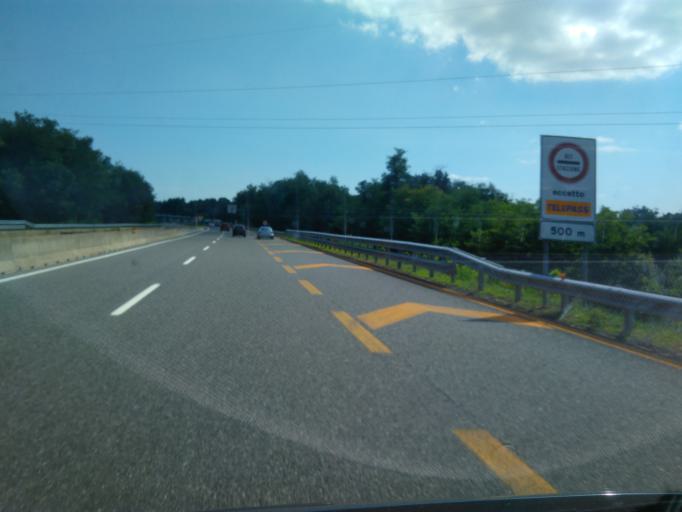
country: IT
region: Piedmont
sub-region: Provincia di Novara
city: Paruzzaro
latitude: 45.7449
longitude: 8.5027
